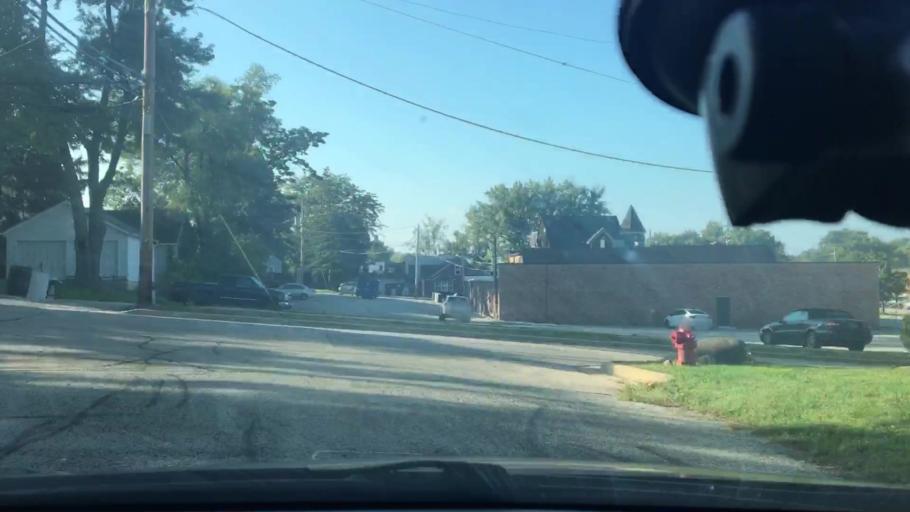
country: US
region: Illinois
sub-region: Kane County
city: East Dundee
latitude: 42.1003
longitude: -88.2742
